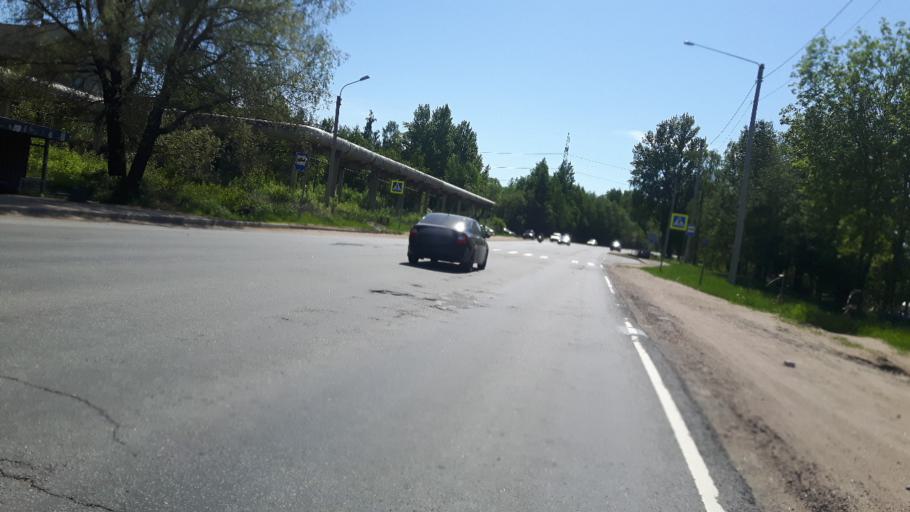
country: RU
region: Leningrad
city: Sosnovyy Bor
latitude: 59.8590
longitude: 29.0629
